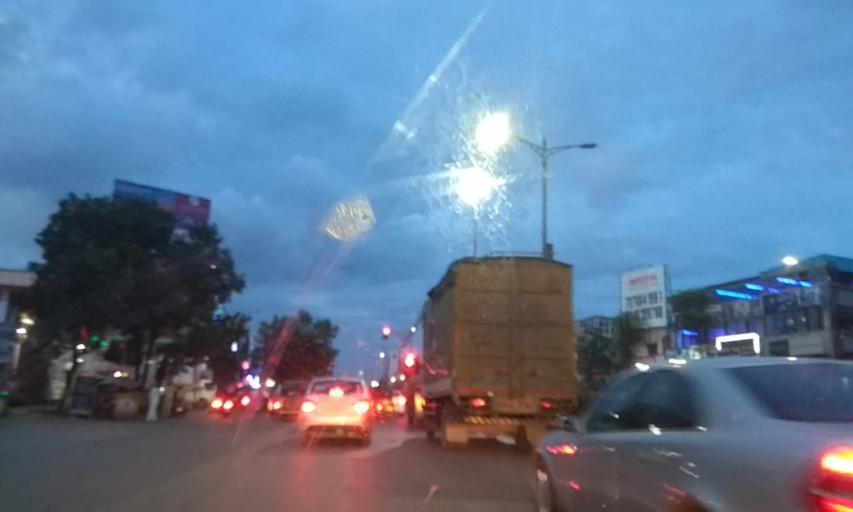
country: IN
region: Maharashtra
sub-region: Pune Division
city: Lohogaon
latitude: 18.5397
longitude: 73.9345
